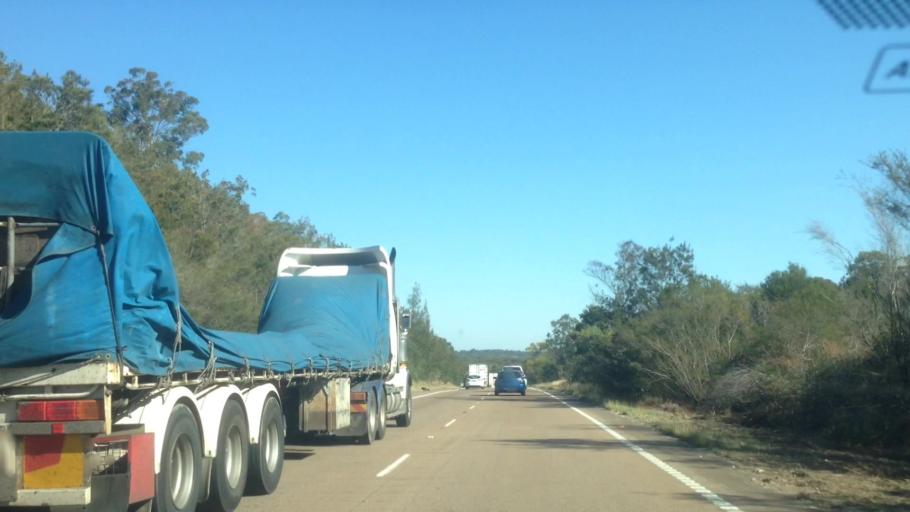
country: AU
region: New South Wales
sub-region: Lake Macquarie Shire
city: Dora Creek
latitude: -33.1509
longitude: 151.4730
